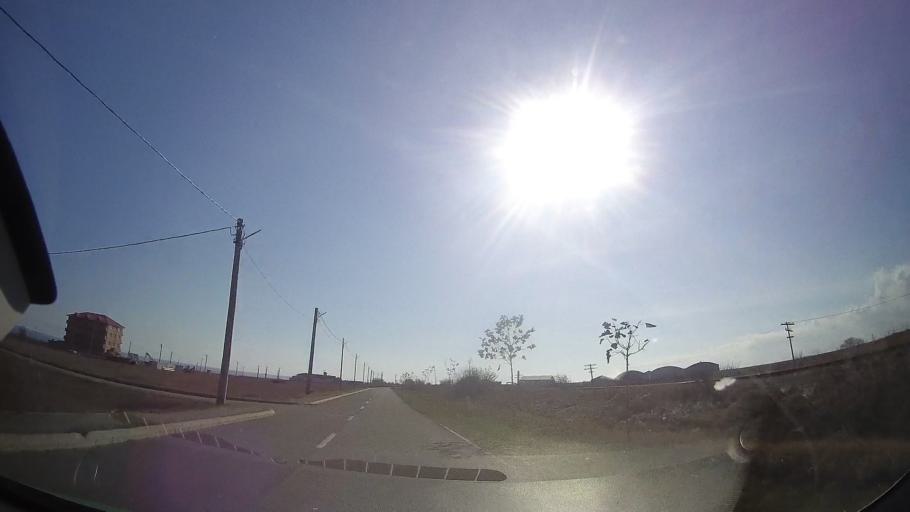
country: RO
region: Constanta
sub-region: Comuna Costinesti
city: Schitu
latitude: 43.9284
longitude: 28.6321
